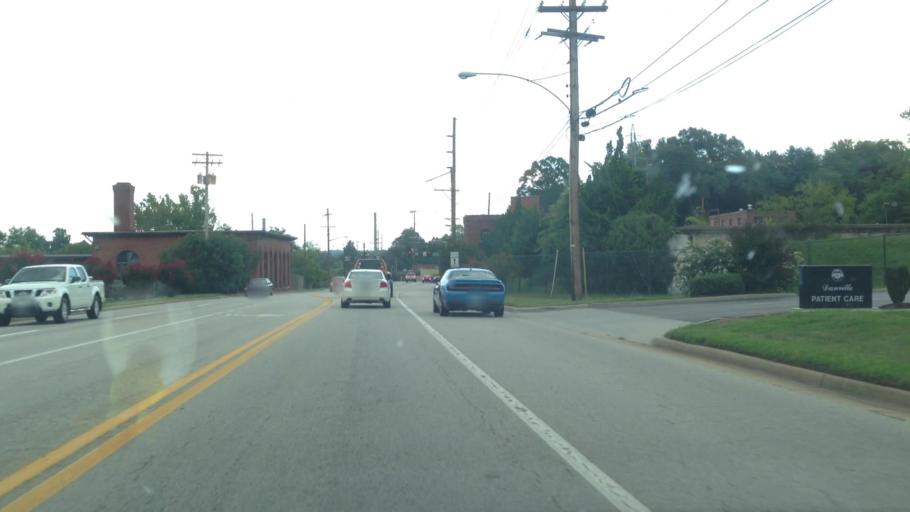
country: US
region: Virginia
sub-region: City of Danville
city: Danville
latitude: 36.5758
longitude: -79.4329
